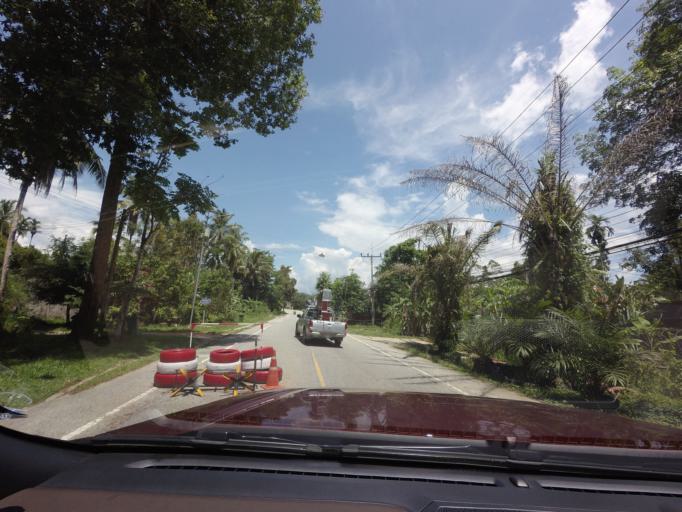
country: TH
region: Narathiwat
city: Chanae
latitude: 6.1328
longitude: 101.6980
